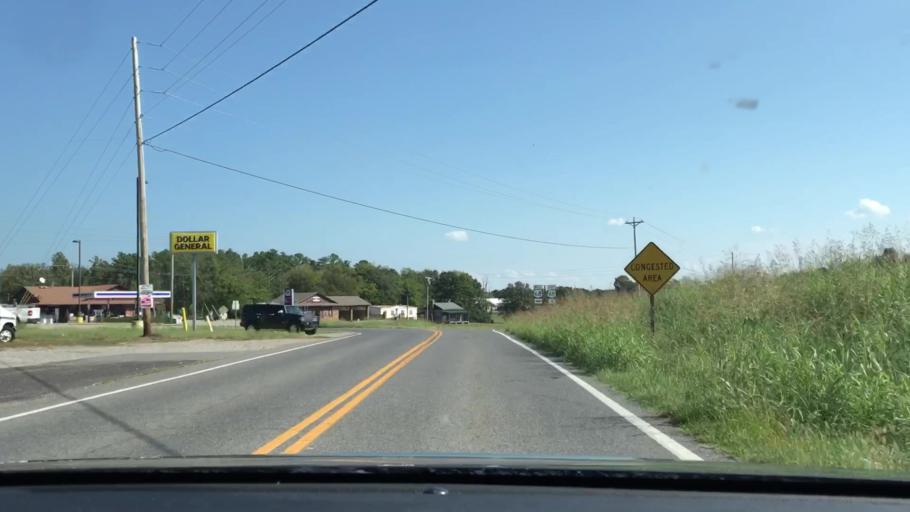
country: US
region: Kentucky
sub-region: Marshall County
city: Benton
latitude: 36.7760
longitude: -88.1596
